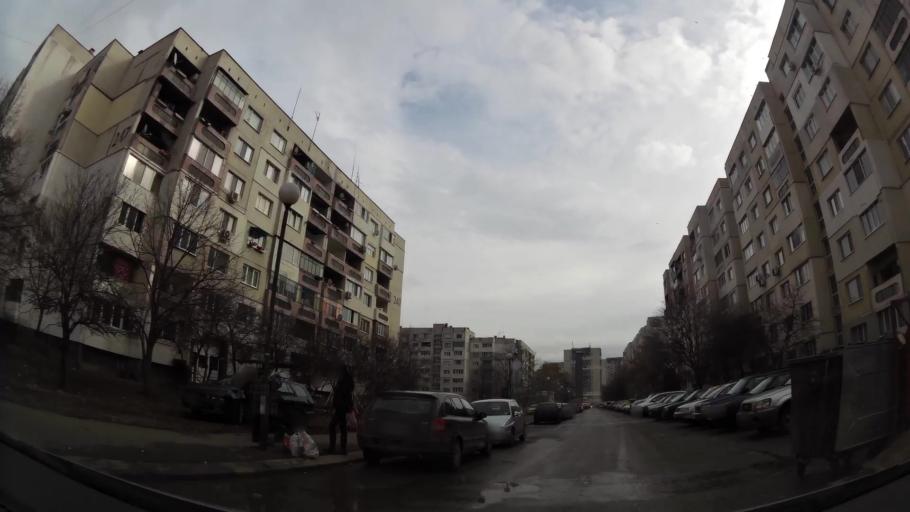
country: BG
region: Sofia-Capital
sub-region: Stolichna Obshtina
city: Sofia
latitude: 42.7467
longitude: 23.2778
